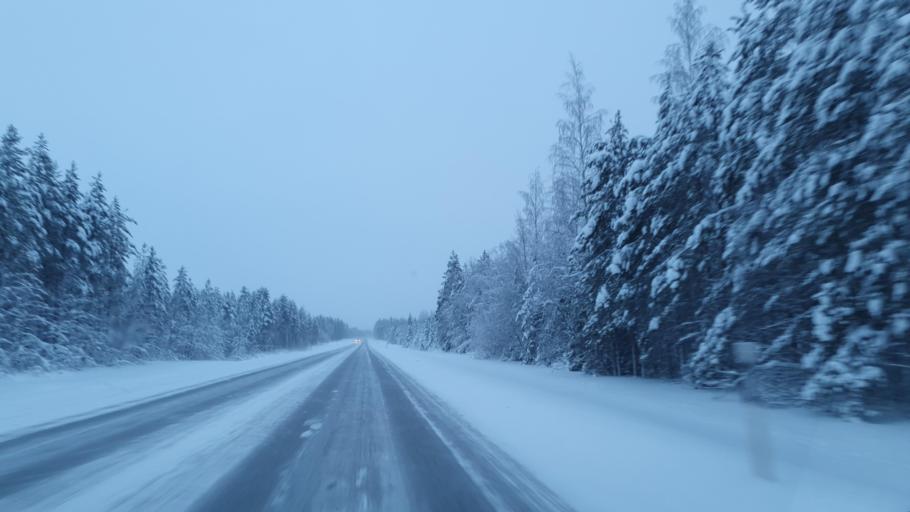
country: FI
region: Kainuu
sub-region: Kajaani
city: Vaala
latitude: 64.5521
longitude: 27.0571
